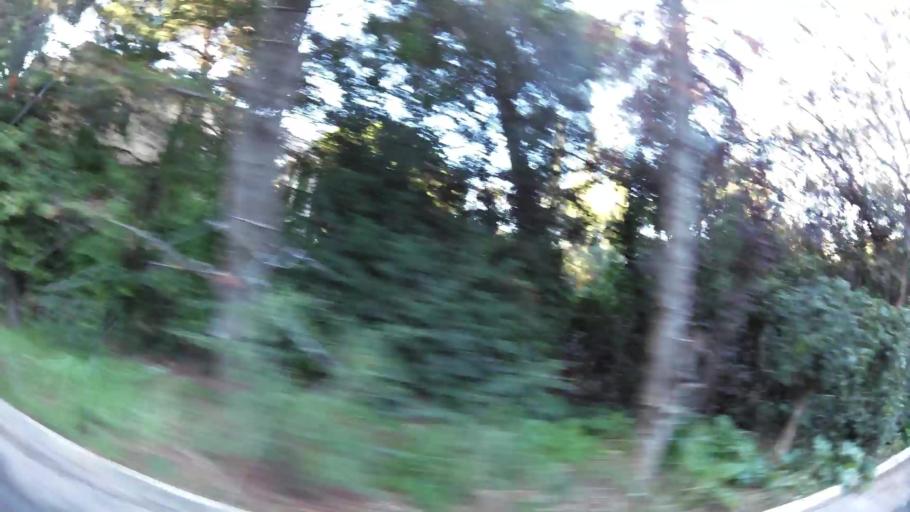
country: GR
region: Attica
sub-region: Nomarchia Athinas
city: Ekali
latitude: 38.0999
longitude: 23.8356
